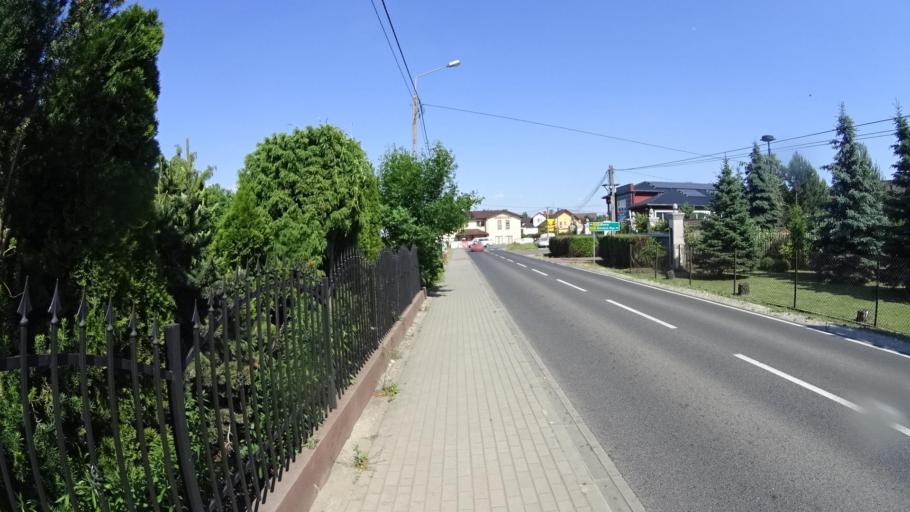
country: PL
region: Masovian Voivodeship
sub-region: Powiat warszawski zachodni
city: Blonie
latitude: 52.1710
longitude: 20.6101
